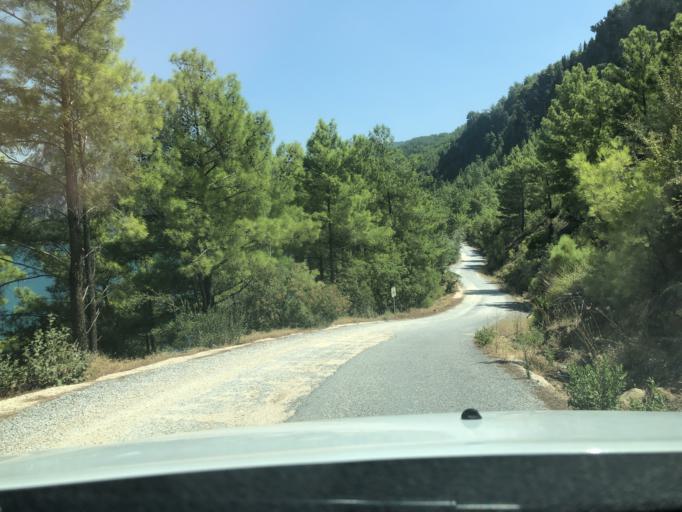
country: TR
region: Antalya
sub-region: Manavgat
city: Manavgat
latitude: 36.9107
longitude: 31.5500
